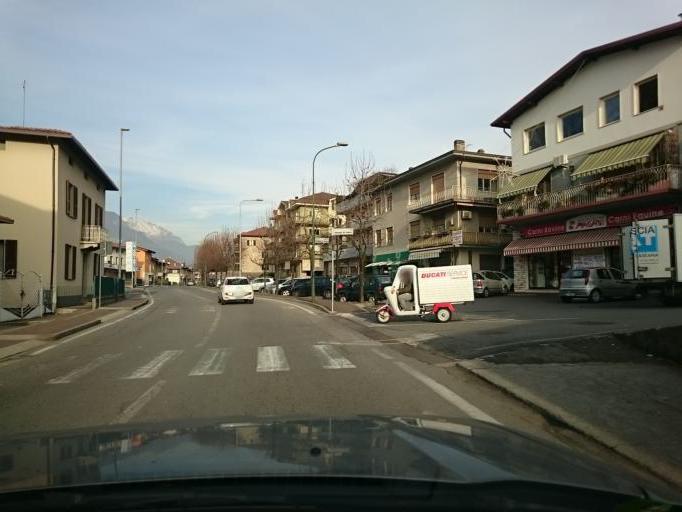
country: IT
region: Lombardy
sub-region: Provincia di Brescia
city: Darfo
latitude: 45.8756
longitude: 10.1774
